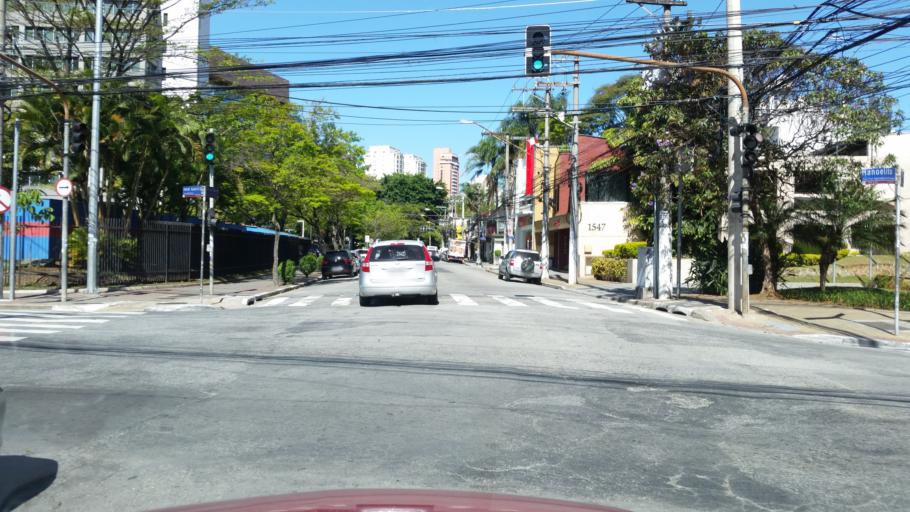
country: BR
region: Sao Paulo
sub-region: Taboao Da Serra
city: Taboao da Serra
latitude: -23.6312
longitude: -46.7101
